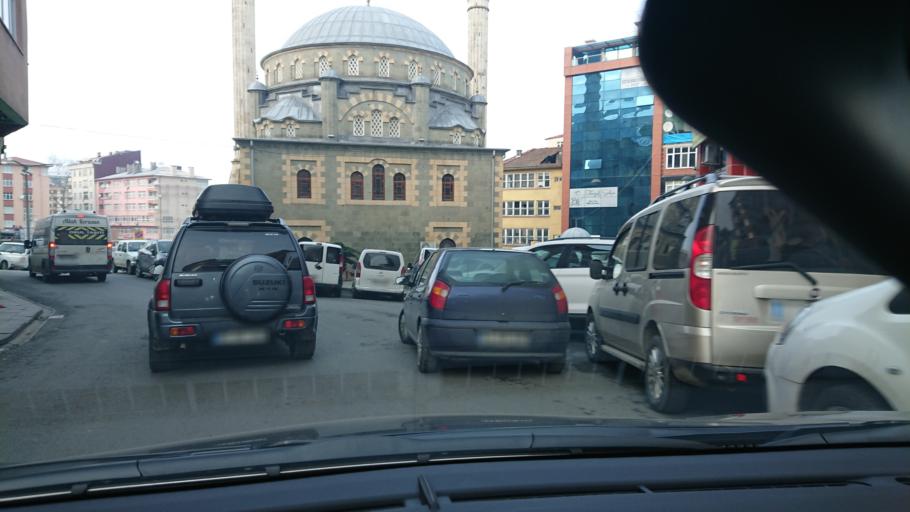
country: TR
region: Rize
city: Rize
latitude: 41.0244
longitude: 40.5166
